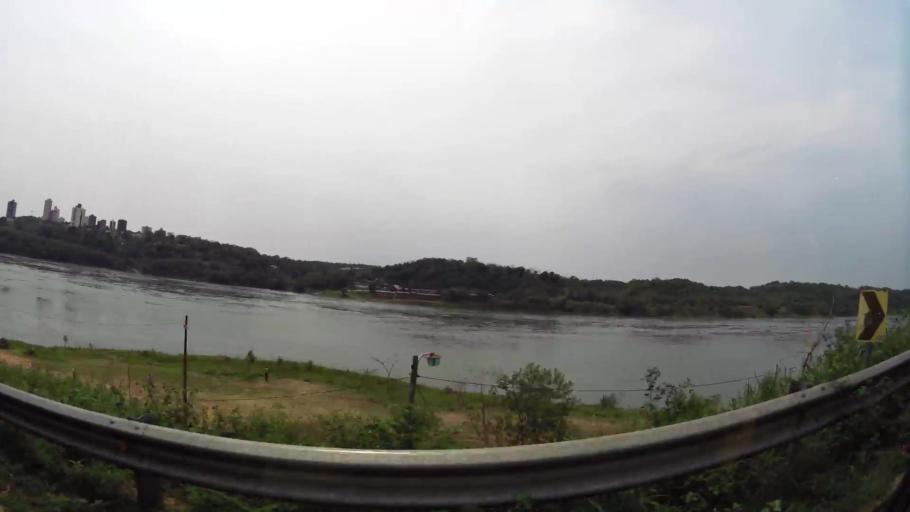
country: BR
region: Parana
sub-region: Foz Do Iguacu
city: Foz do Iguacu
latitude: -25.5566
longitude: -54.5977
